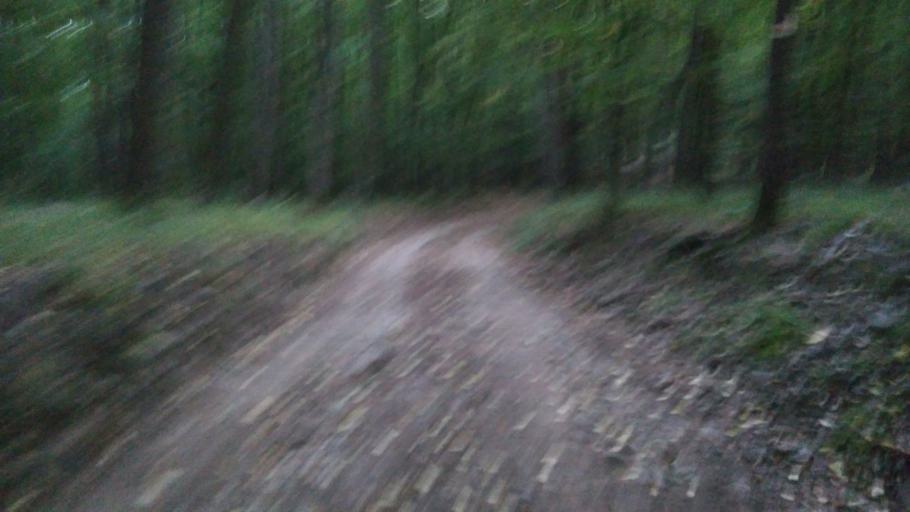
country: SK
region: Nitriansky
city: Sahy
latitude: 47.9971
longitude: 18.9529
